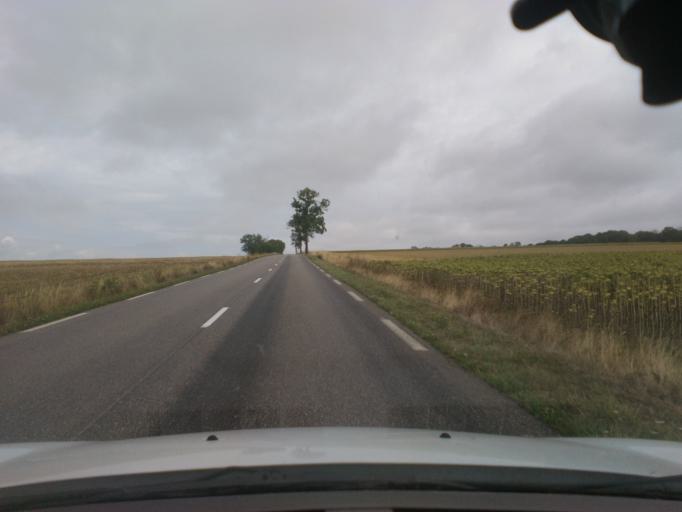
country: FR
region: Lorraine
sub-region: Departement de Meurthe-et-Moselle
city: Vezelise
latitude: 48.4368
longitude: 6.1255
